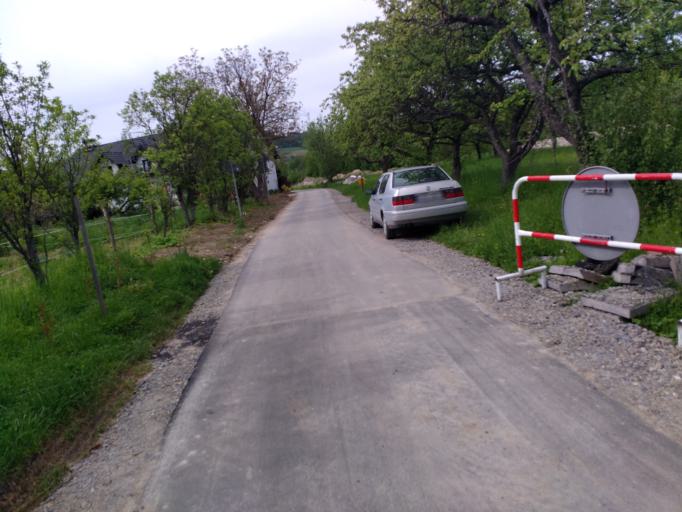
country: PL
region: Lesser Poland Voivodeship
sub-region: Powiat nowosadecki
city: Lacko
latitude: 49.5494
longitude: 20.4317
